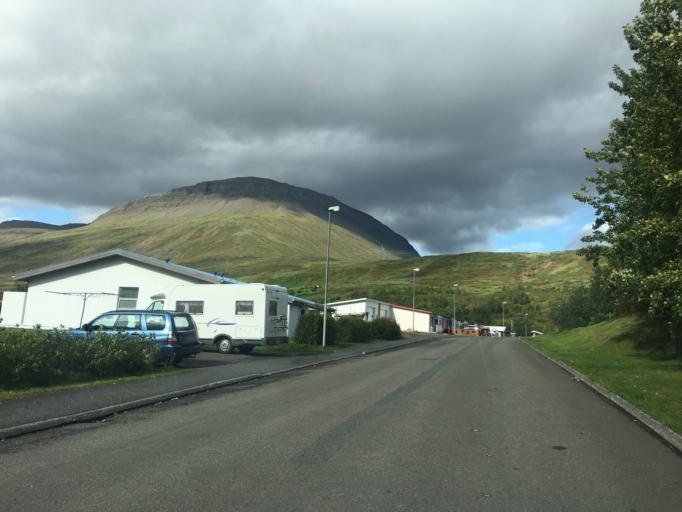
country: IS
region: East
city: Reydarfjoerdur
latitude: 65.0359
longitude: -14.2097
